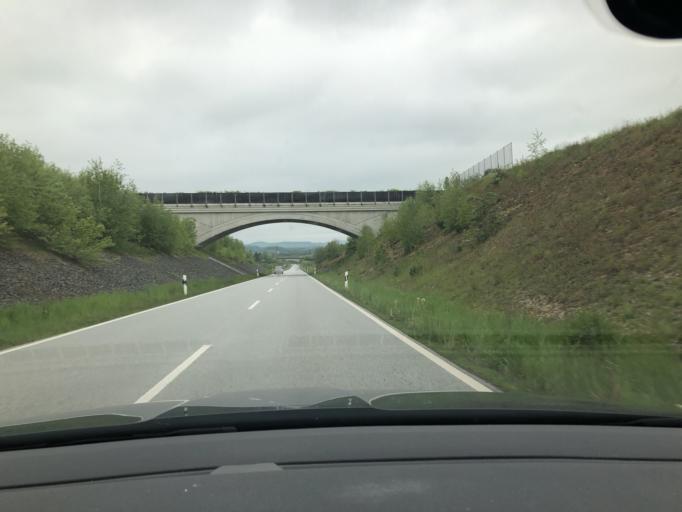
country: DE
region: Saxony
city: Dohma
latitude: 50.8991
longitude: 13.9338
